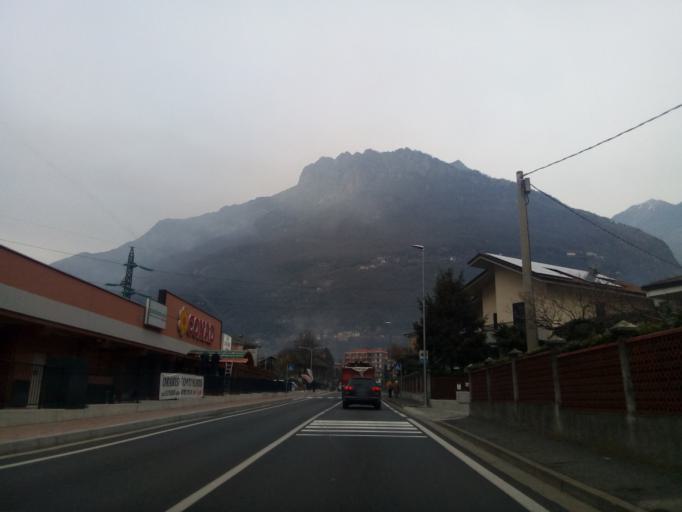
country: IT
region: Aosta Valley
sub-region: Valle d'Aosta
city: Pont-Saint-Martin
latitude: 45.5934
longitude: 7.7991
